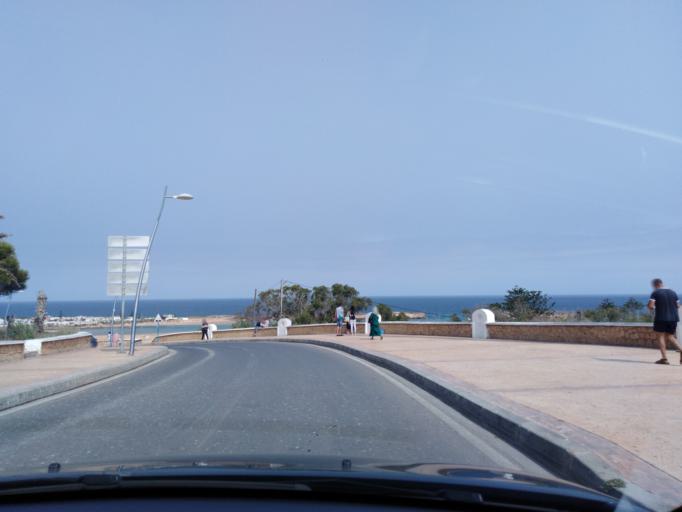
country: MA
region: Doukkala-Abda
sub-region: Safi
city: Safi
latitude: 32.7346
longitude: -9.0339
